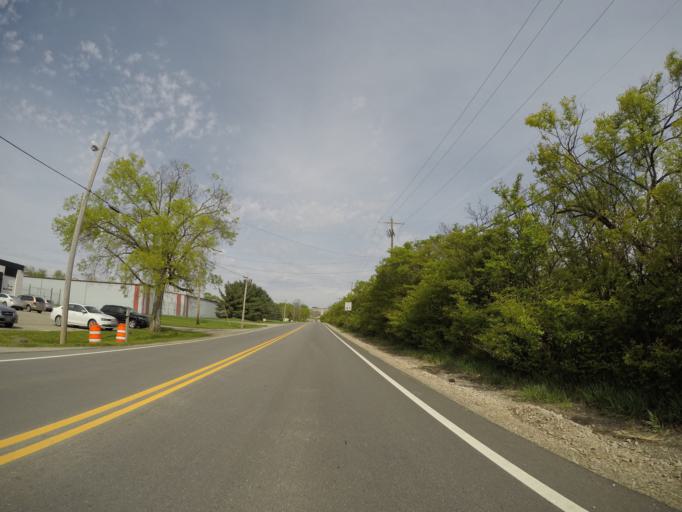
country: US
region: Ohio
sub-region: Franklin County
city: Upper Arlington
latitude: 39.9969
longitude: -83.0875
